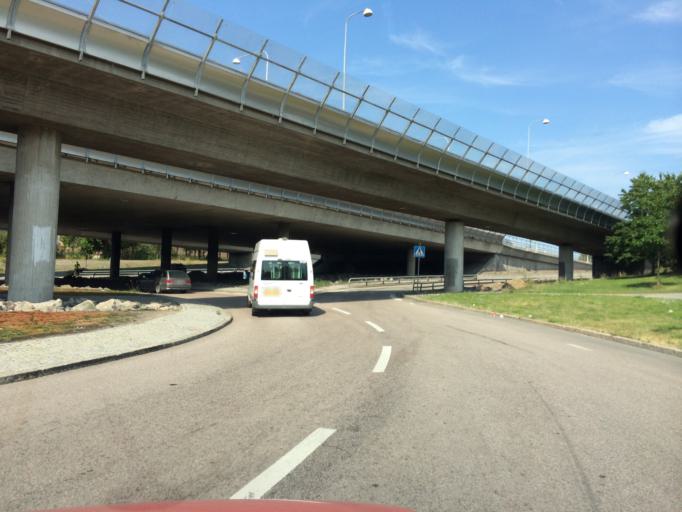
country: SE
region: Stockholm
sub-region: Stockholms Kommun
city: Arsta
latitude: 59.2952
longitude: 18.0034
